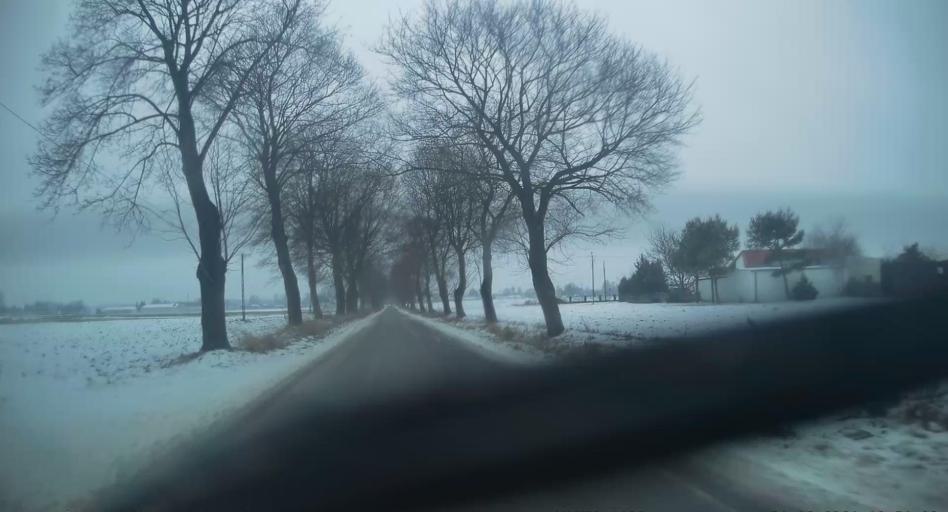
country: PL
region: Lodz Voivodeship
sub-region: Powiat tomaszowski
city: Czerniewice
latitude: 51.6832
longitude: 20.2182
